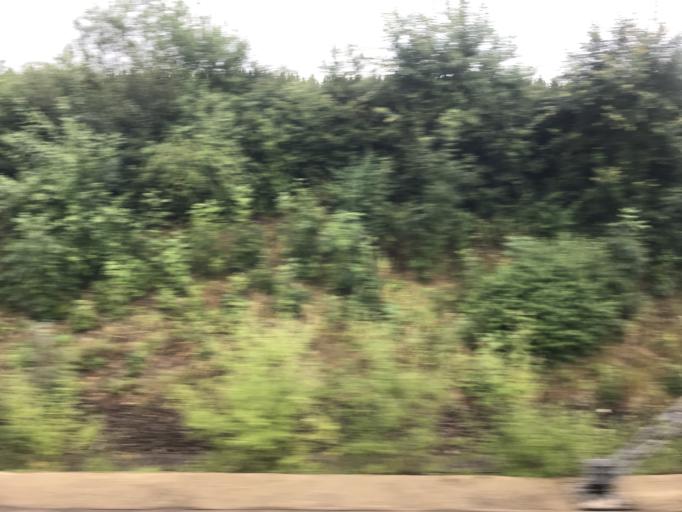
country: LU
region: Luxembourg
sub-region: Canton d'Esch-sur-Alzette
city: Reckange-sur-Mess
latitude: 49.5791
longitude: 6.0083
